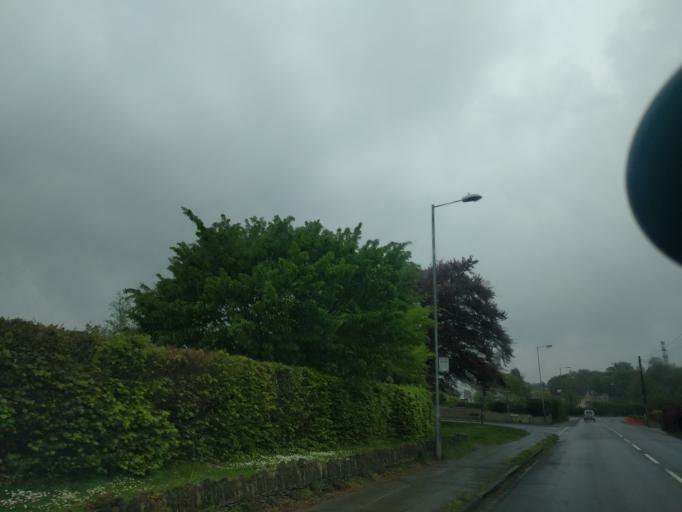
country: GB
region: England
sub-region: Wiltshire
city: Chippenham
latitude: 51.4700
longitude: -2.1241
